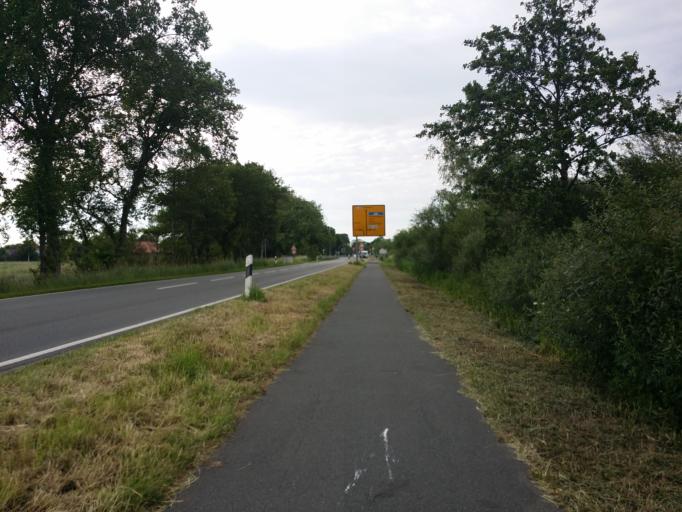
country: DE
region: Lower Saxony
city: Wittmund
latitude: 53.5653
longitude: 7.7839
